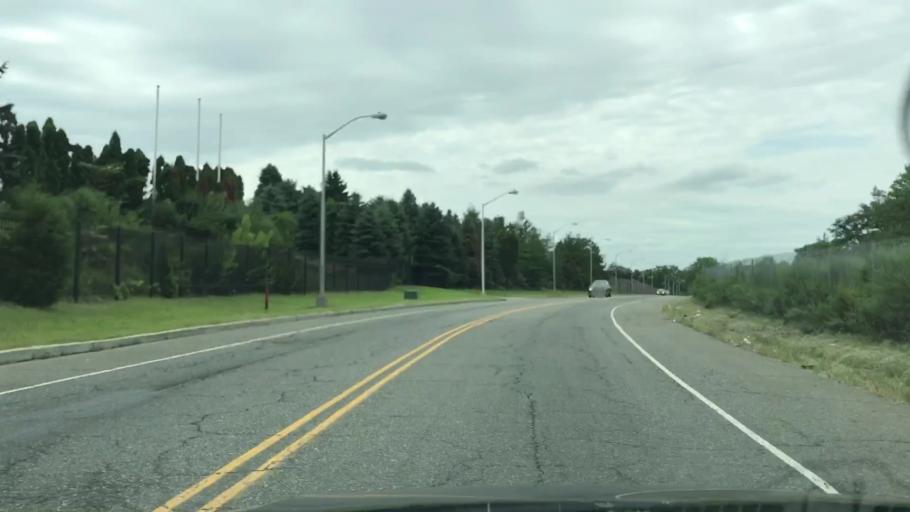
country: US
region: New Jersey
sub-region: Hudson County
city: Jersey City
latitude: 40.6993
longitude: -74.0698
